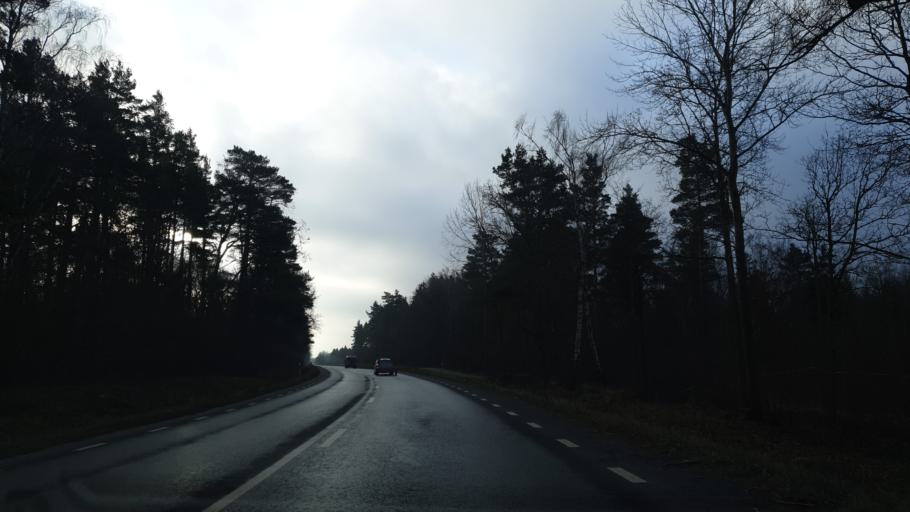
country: SE
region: Blekinge
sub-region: Karlshamns Kommun
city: Morrum
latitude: 56.1475
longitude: 14.6685
